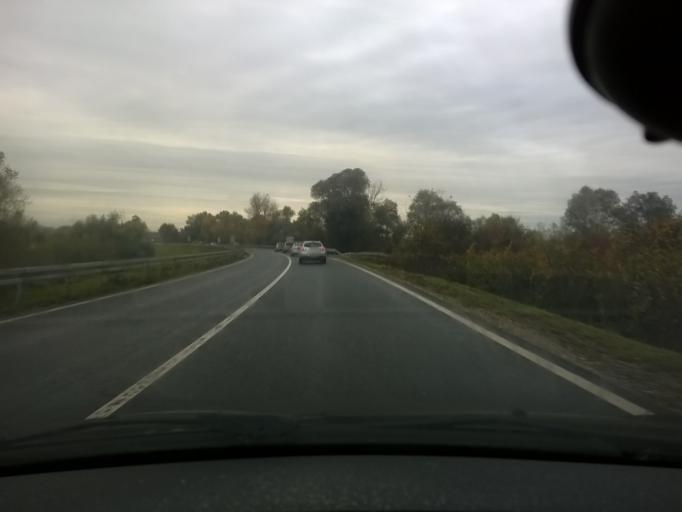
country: HR
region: Zagrebacka
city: Pojatno
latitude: 45.9249
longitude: 15.8233
